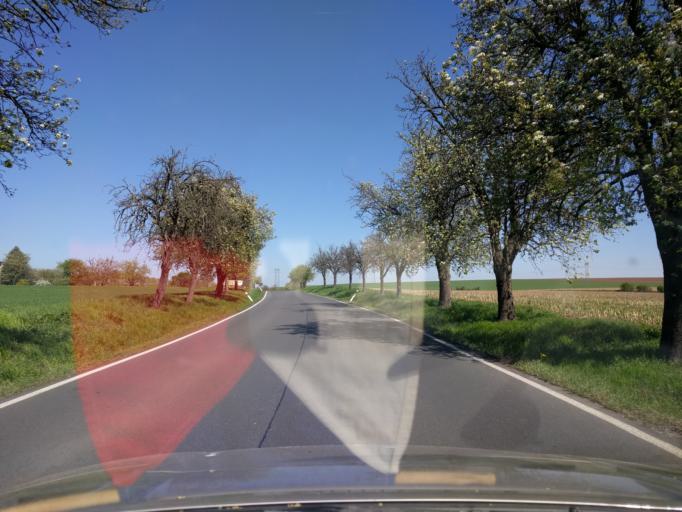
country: CZ
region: Central Bohemia
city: Cesky Brod
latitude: 50.0936
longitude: 14.8645
